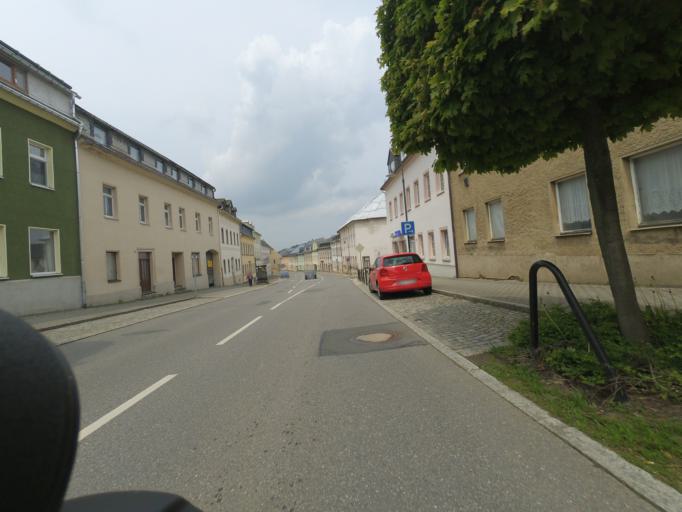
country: DE
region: Saxony
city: Zoblitz
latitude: 50.6574
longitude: 13.2342
